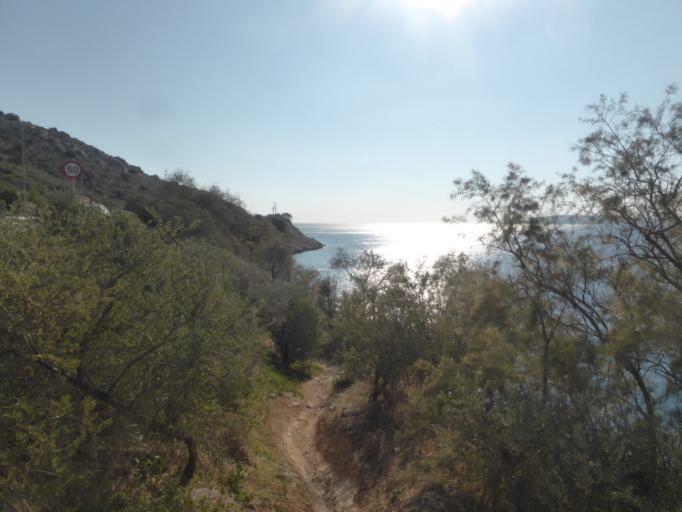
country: GR
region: Attica
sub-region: Nomarchia Anatolikis Attikis
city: Vouliagmeni
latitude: 37.8069
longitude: 23.7842
